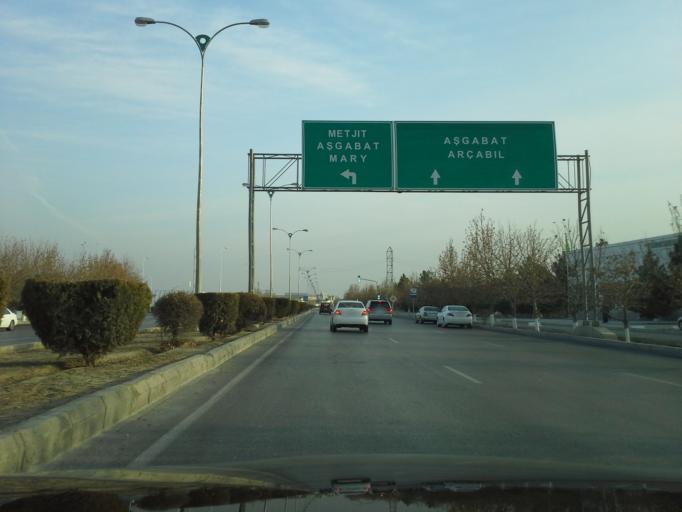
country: TM
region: Ahal
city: Abadan
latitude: 38.0529
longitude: 58.1836
